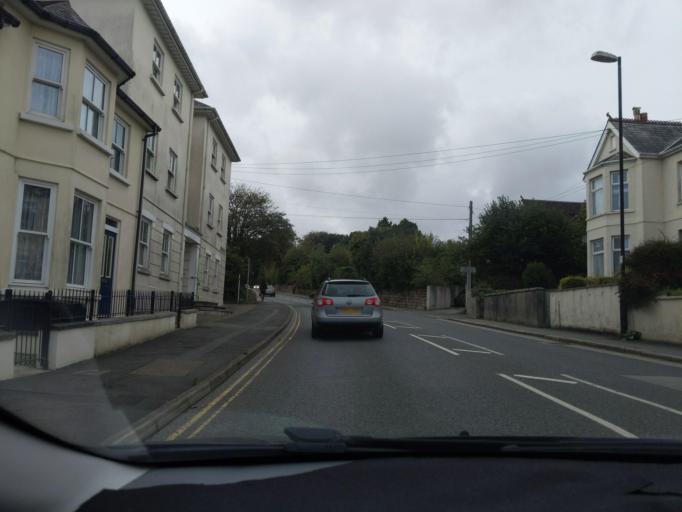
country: GB
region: England
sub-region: Cornwall
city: St Austell
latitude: 50.3413
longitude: -4.7803
